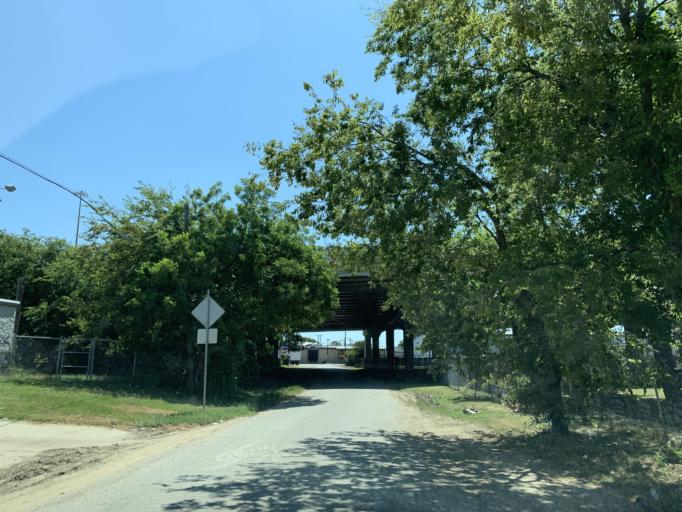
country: US
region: Texas
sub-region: Dallas County
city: Dallas
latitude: 32.7856
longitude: -96.7688
